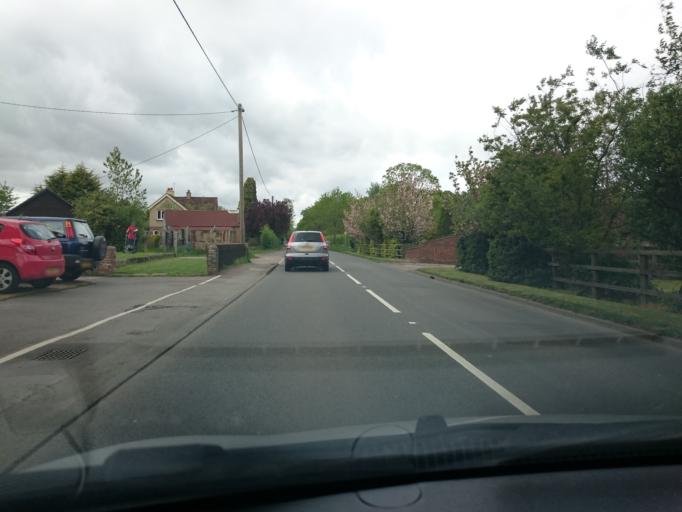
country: GB
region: England
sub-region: Surrey
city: Normandy
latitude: 51.2569
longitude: -0.6659
